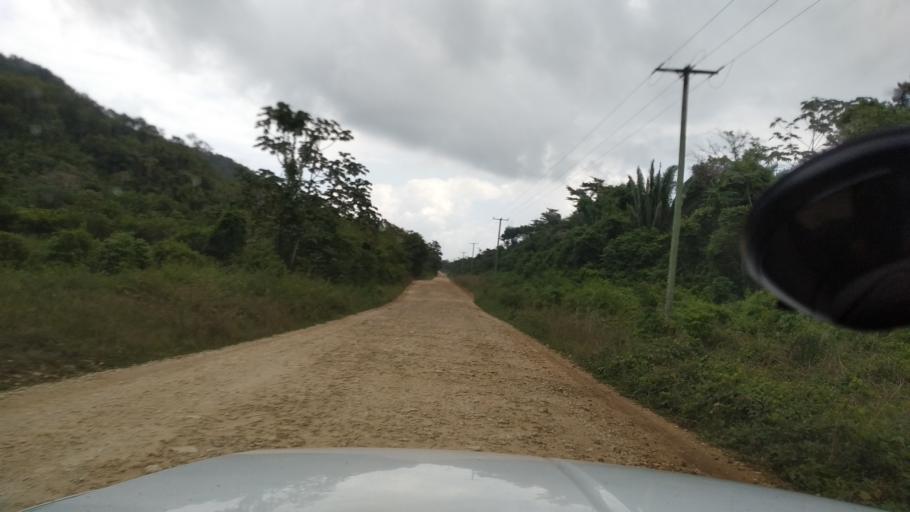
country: BZ
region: Toledo
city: Punta Gorda
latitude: 16.2130
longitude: -89.0163
